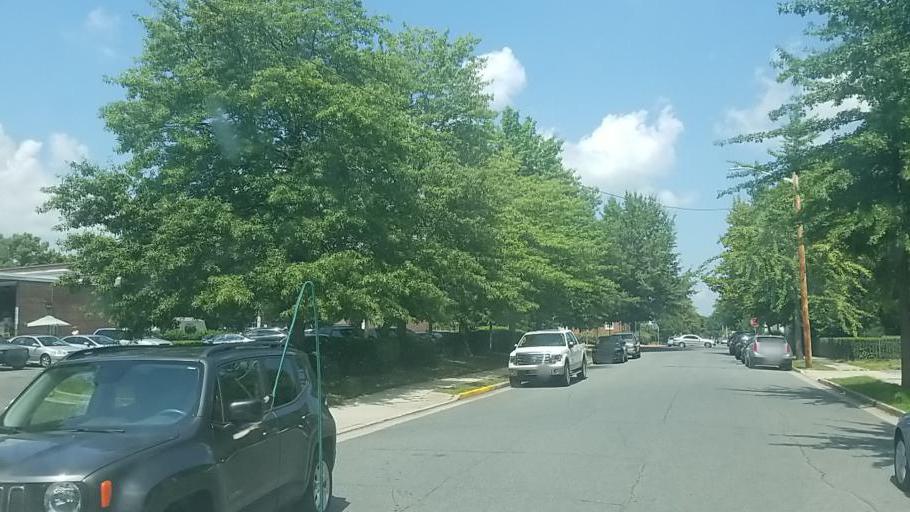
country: US
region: Maryland
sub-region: Talbot County
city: Easton
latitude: 38.7733
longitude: -76.0730
